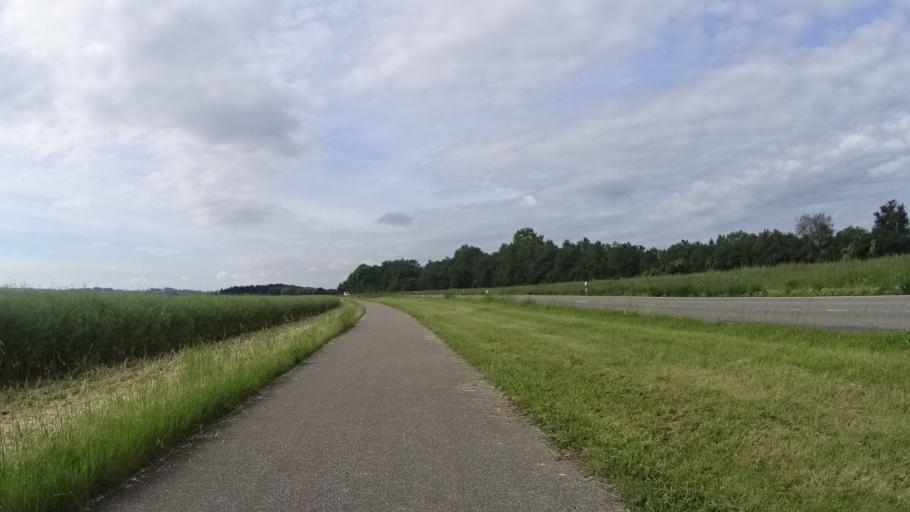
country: DE
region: Baden-Wuerttemberg
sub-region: Freiburg Region
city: Neuenburg am Rhein
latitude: 47.7947
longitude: 7.5560
